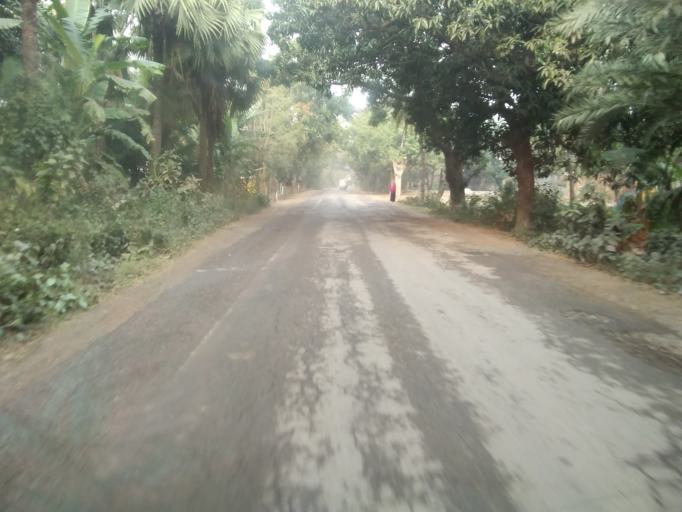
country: BD
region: Khulna
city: Satkhira
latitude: 22.6861
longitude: 89.0300
